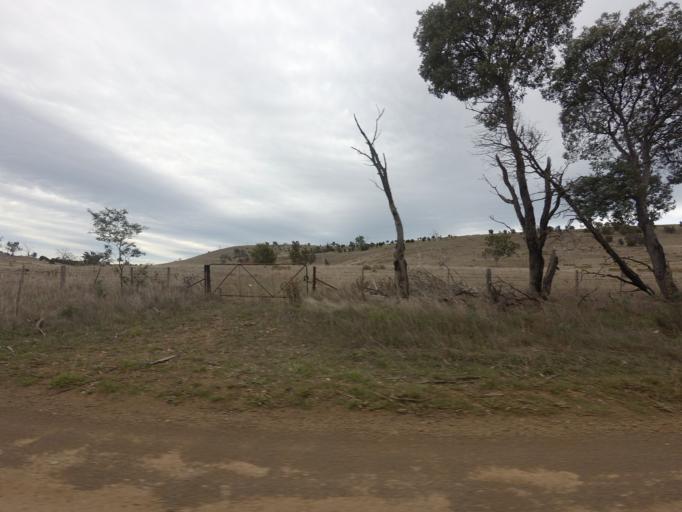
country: AU
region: Tasmania
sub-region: Derwent Valley
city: New Norfolk
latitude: -42.5559
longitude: 146.9139
